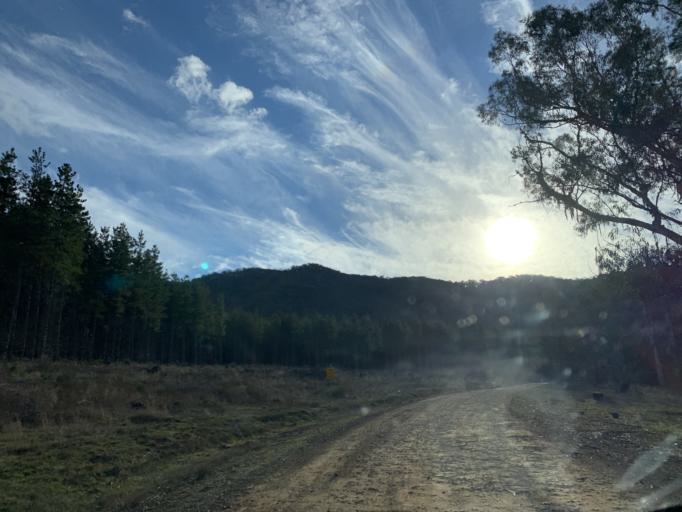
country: AU
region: Victoria
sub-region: Mansfield
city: Mansfield
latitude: -36.9353
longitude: 146.0946
